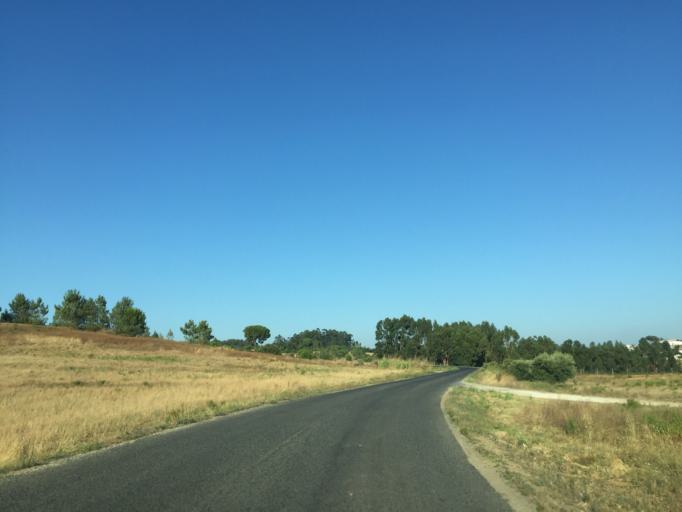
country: PT
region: Lisbon
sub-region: Azambuja
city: Aveiras de Cima
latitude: 39.1316
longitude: -8.9420
